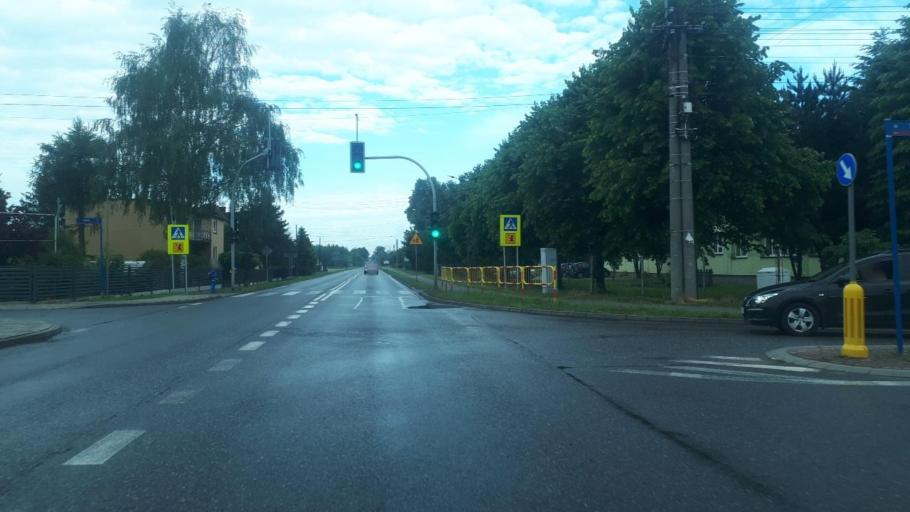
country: PL
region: Silesian Voivodeship
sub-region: Powiat pszczynski
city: Gora
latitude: 49.9725
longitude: 19.1024
